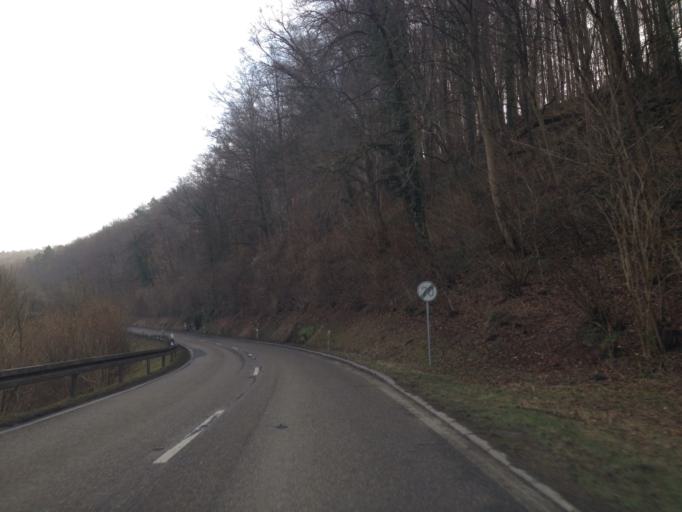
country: DE
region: Baden-Wuerttemberg
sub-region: Regierungsbezirk Stuttgart
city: Jagsthausen
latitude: 49.3330
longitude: 9.5114
